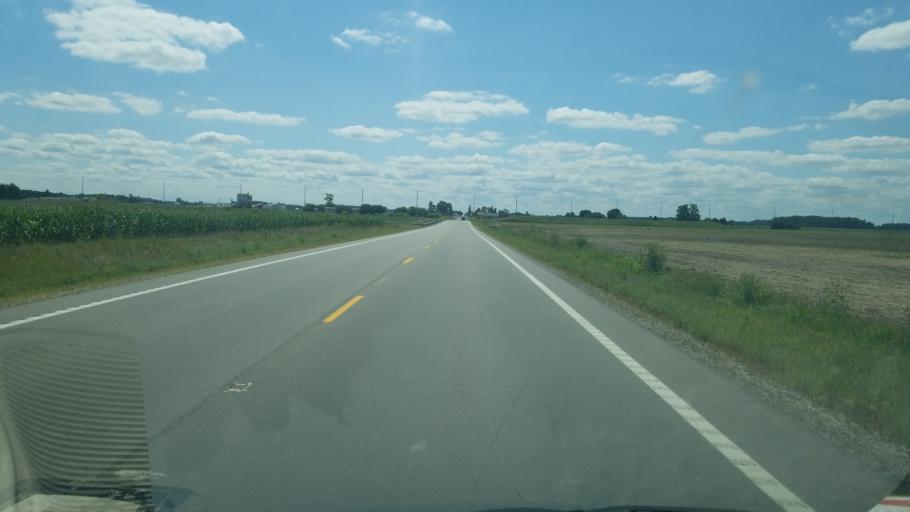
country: US
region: Ohio
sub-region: Fulton County
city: Delta
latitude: 41.7072
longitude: -84.0371
